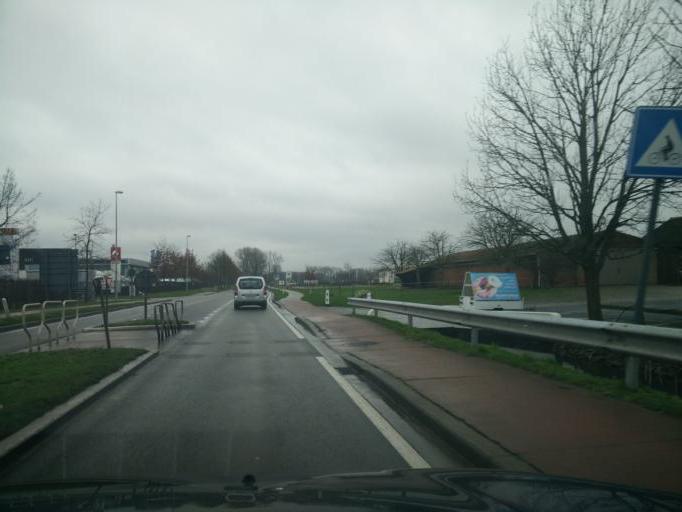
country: BE
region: Flanders
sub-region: Provincie Oost-Vlaanderen
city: Lochristi
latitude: 51.1047
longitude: 3.8694
